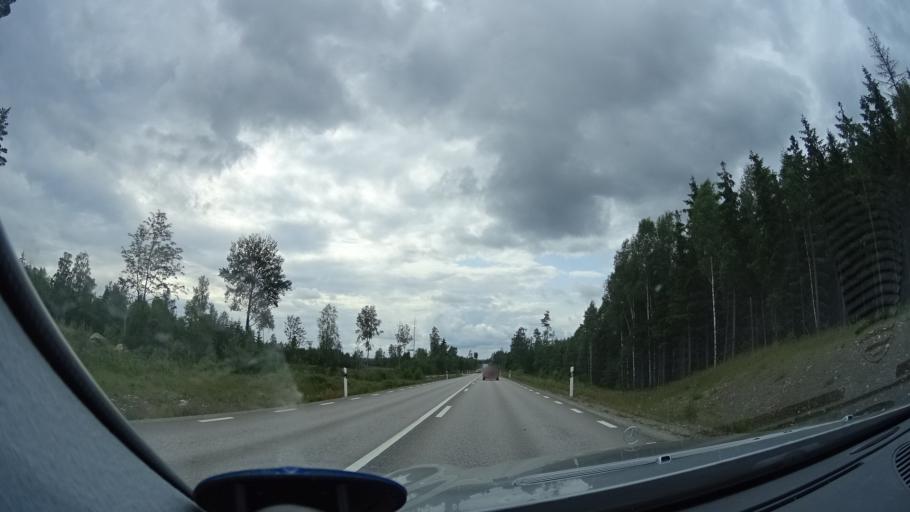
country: SE
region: Kronoberg
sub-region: Tingsryds Kommun
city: Tingsryd
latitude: 56.5094
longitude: 15.0193
